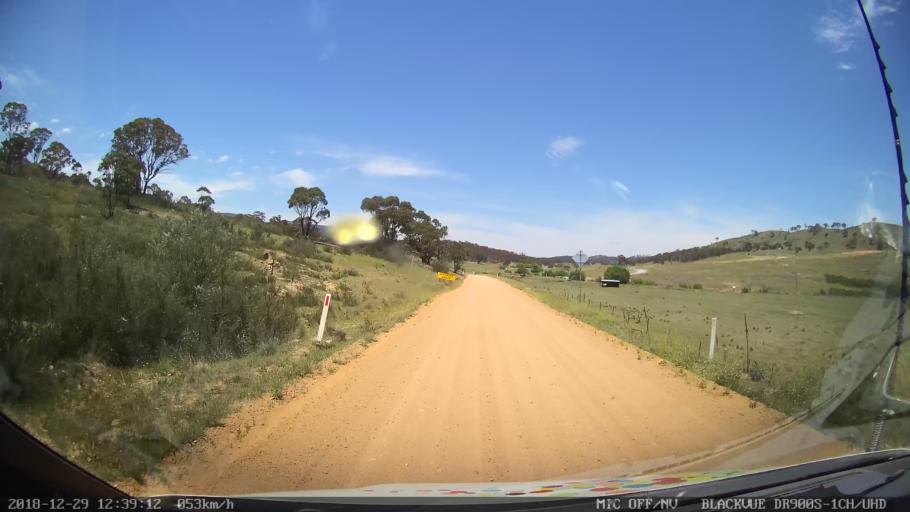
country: AU
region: Australian Capital Territory
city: Macarthur
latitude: -35.5955
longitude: 149.2278
